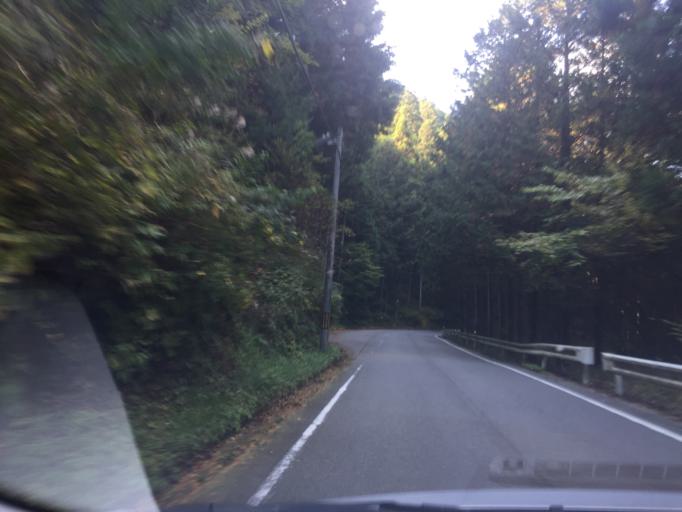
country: JP
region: Aichi
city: Shinshiro
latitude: 35.1233
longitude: 137.6441
